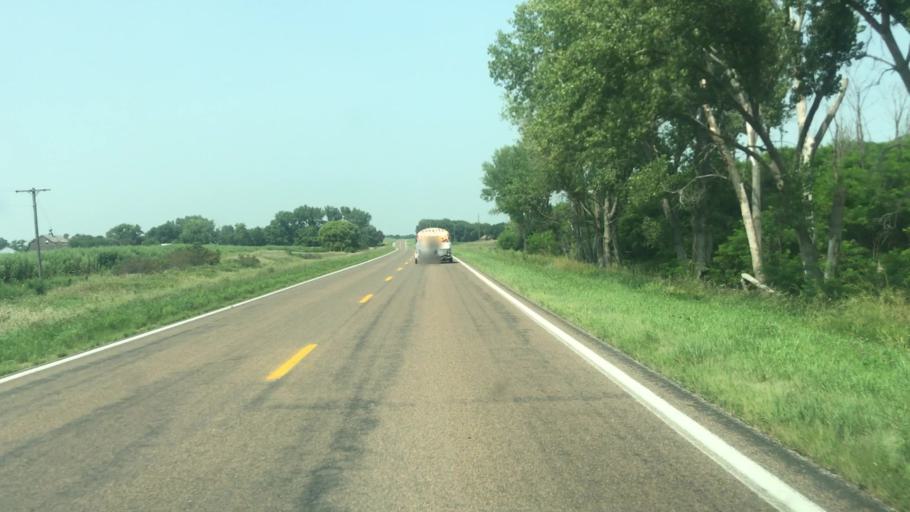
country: US
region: Nebraska
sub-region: Sherman County
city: Loup City
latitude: 41.2433
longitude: -98.9386
